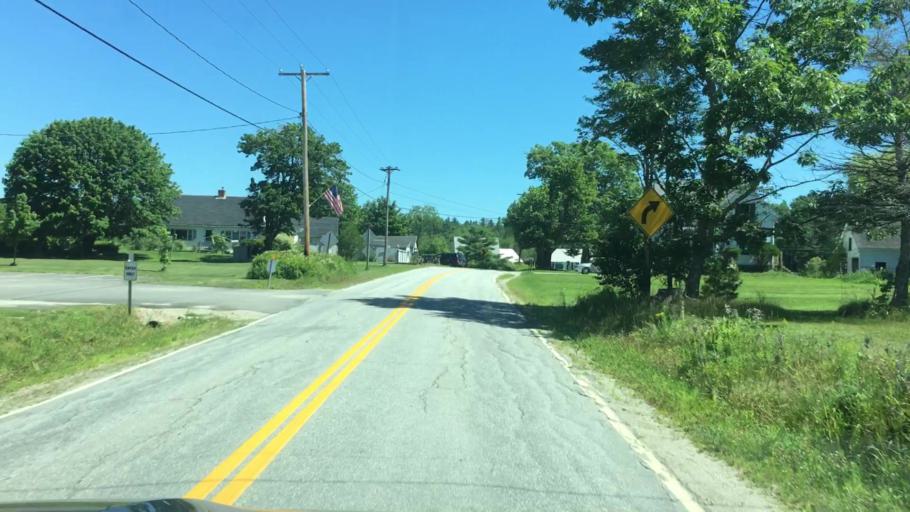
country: US
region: Maine
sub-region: Hancock County
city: Penobscot
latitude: 44.4683
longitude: -68.7086
